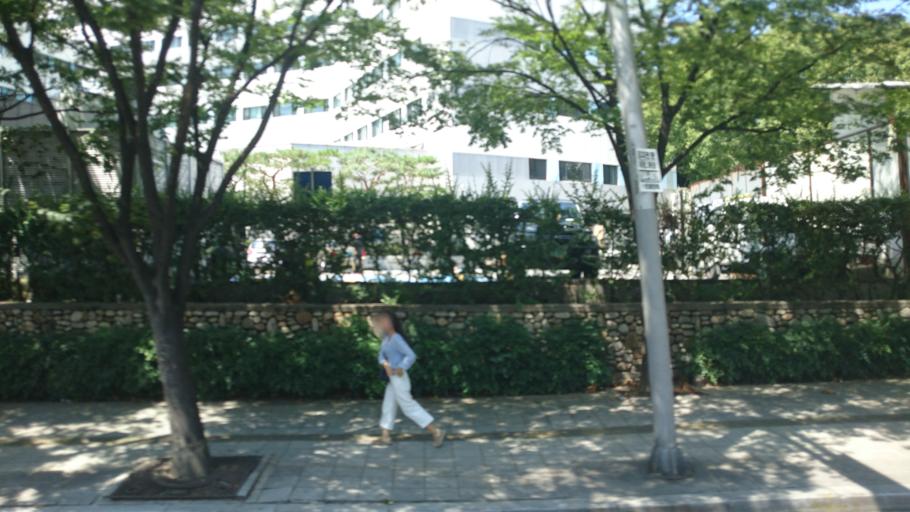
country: KR
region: Daegu
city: Daegu
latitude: 35.8842
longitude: 128.6253
